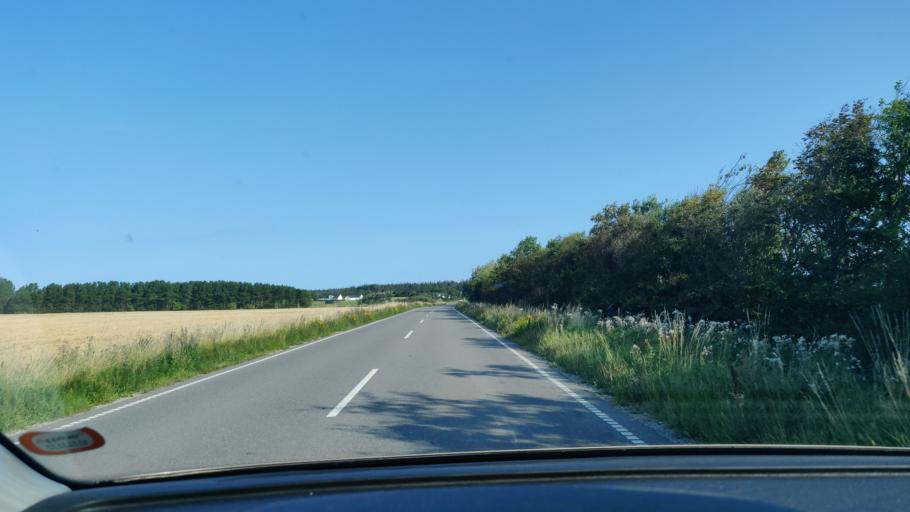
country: DK
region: North Denmark
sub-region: Jammerbugt Kommune
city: Pandrup
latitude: 57.2400
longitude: 9.6491
